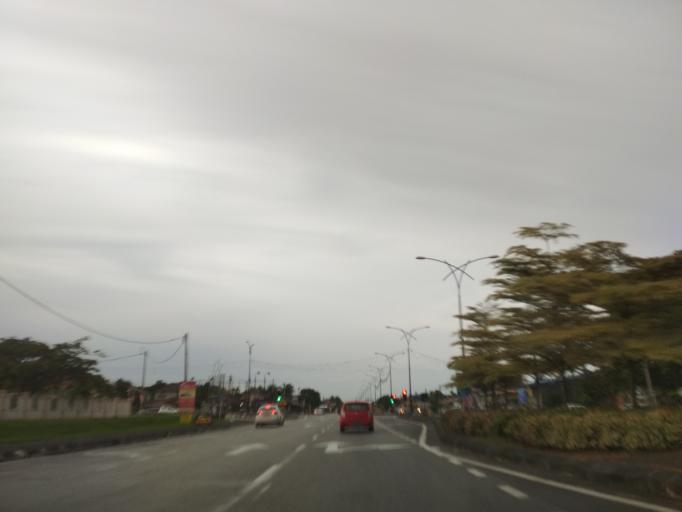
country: MY
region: Perlis
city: Kangar
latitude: 6.4532
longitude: 100.2066
